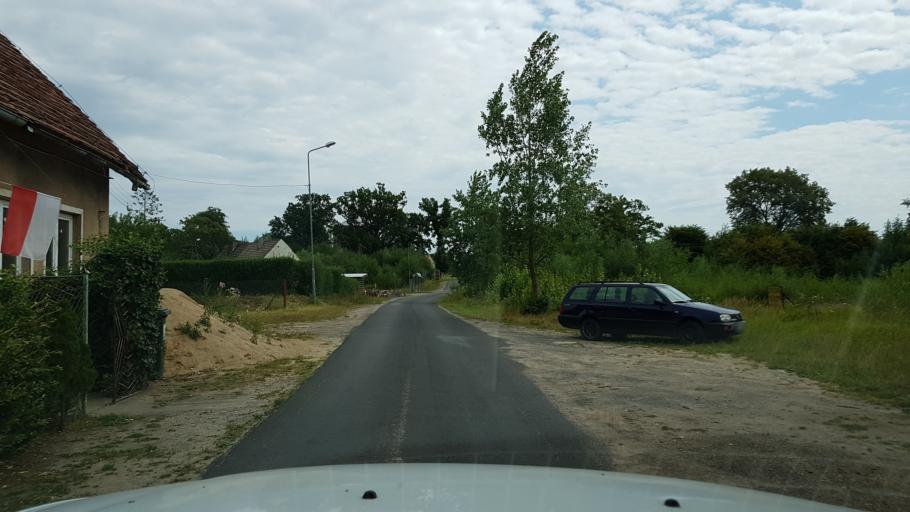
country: PL
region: West Pomeranian Voivodeship
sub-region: Powiat koszalinski
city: Mielno
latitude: 54.1711
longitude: 16.0496
